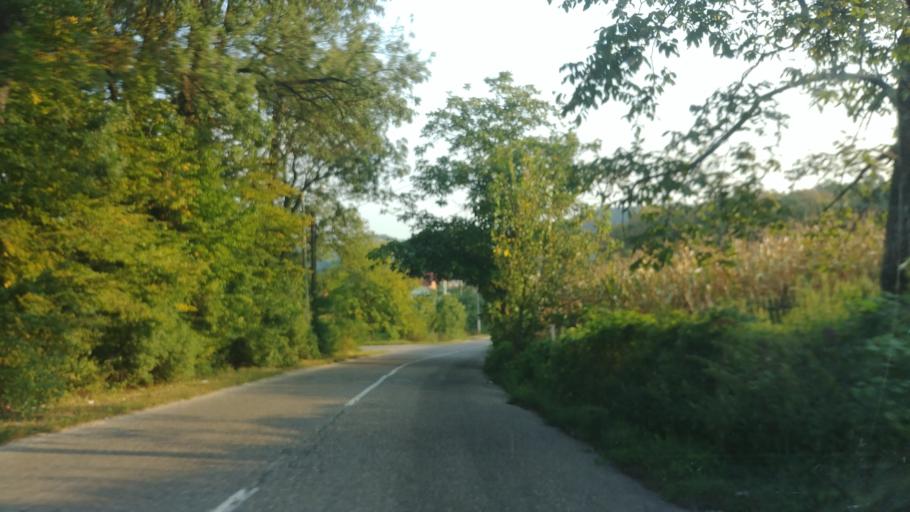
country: BA
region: Republika Srpska
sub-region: Opstina Ugljevik
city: Ugljevik
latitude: 44.6998
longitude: 18.9928
